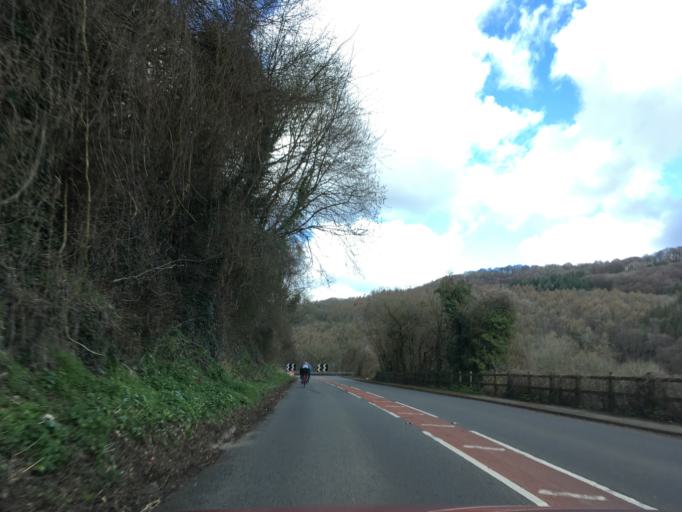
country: GB
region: Wales
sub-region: Monmouthshire
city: Tintern
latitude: 51.6907
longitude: -2.6713
